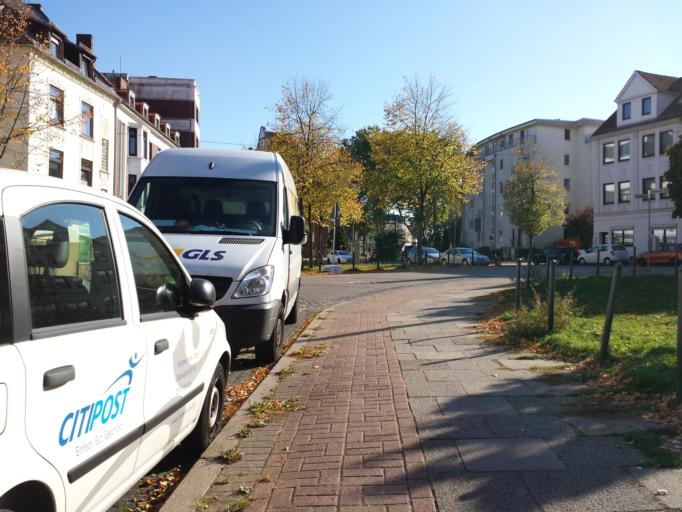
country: DE
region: Bremen
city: Bremen
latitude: 53.0984
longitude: 8.7807
